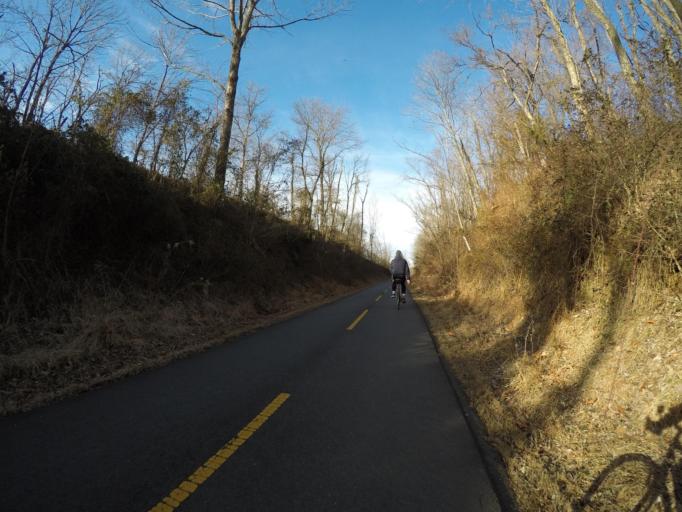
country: US
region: Virginia
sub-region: Loudoun County
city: Leesburg
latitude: 39.1279
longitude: -77.6071
